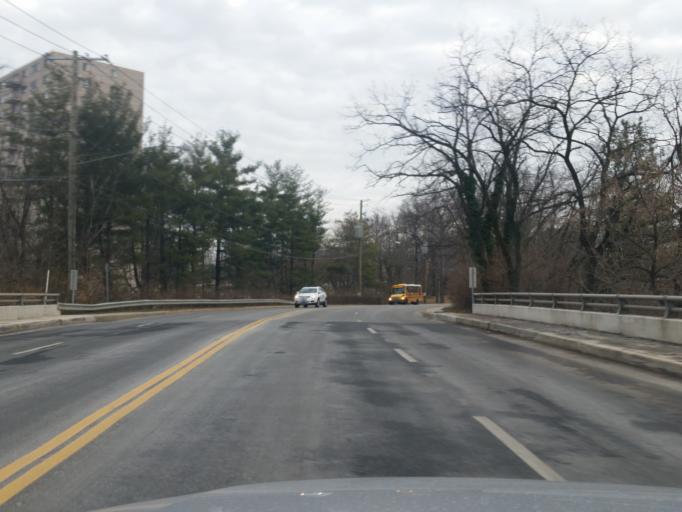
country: US
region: Maryland
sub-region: Montgomery County
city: Forest Glen
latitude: 39.0002
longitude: -77.0541
